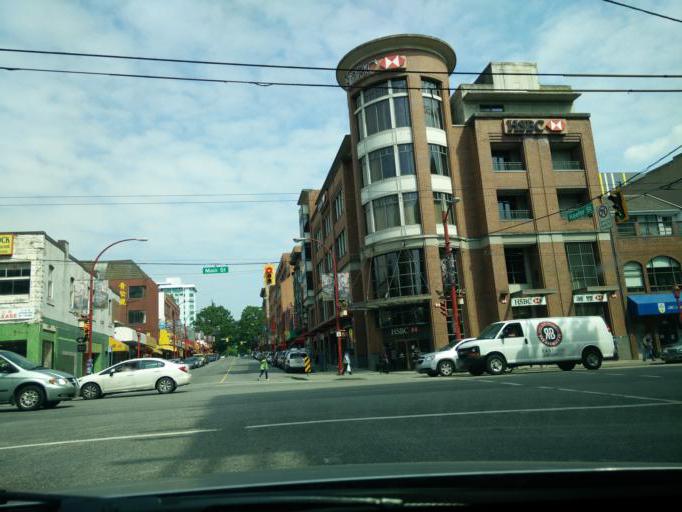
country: CA
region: British Columbia
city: West End
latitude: 49.2795
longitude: -123.1001
